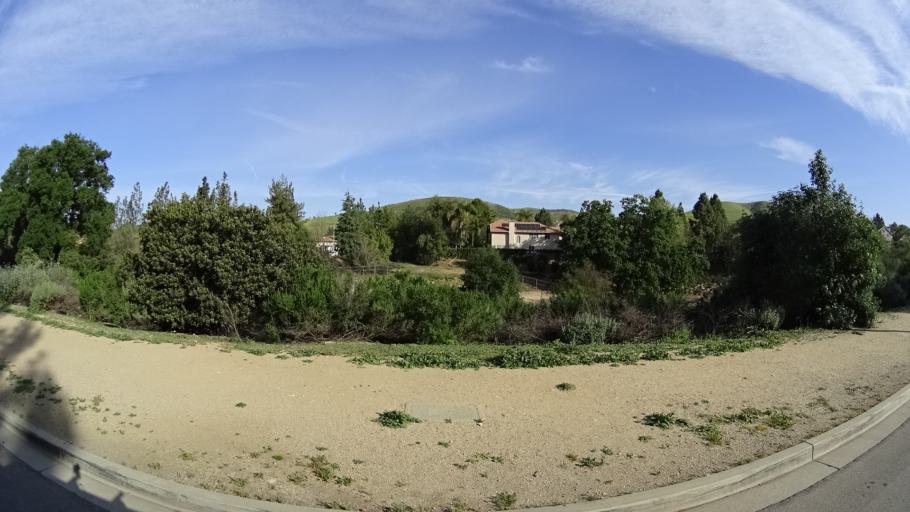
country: US
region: California
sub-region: Ventura County
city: Thousand Oaks
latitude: 34.2116
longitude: -118.8222
